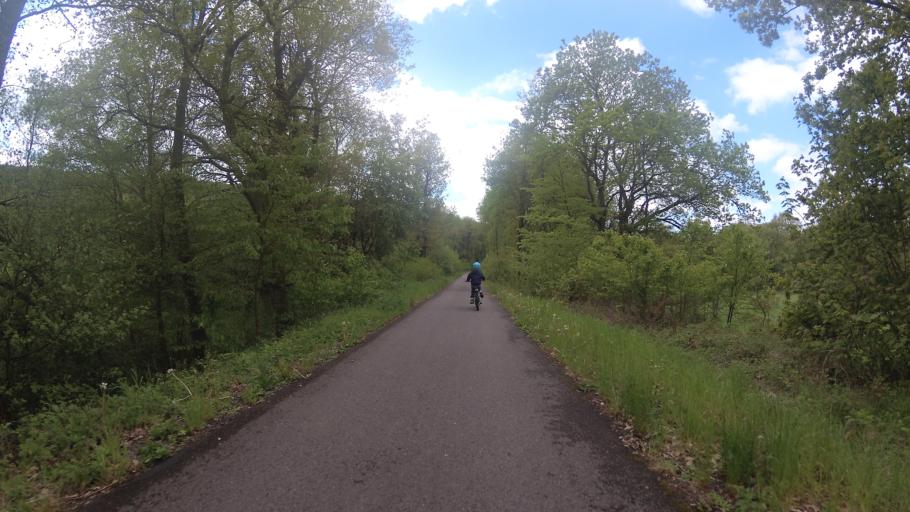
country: DE
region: Saarland
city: Schmelz
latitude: 49.3991
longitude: 6.8610
